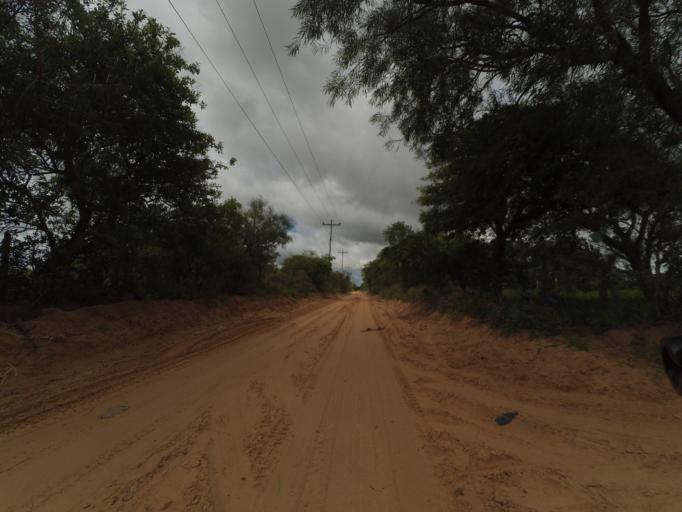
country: BO
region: Santa Cruz
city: Santa Rita
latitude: -17.9069
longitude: -63.2453
